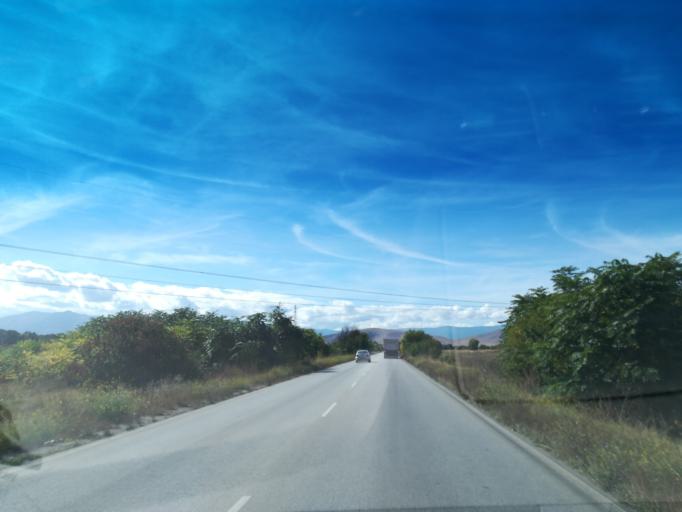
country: BG
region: Plovdiv
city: Stamboliyski
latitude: 42.1158
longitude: 24.5281
